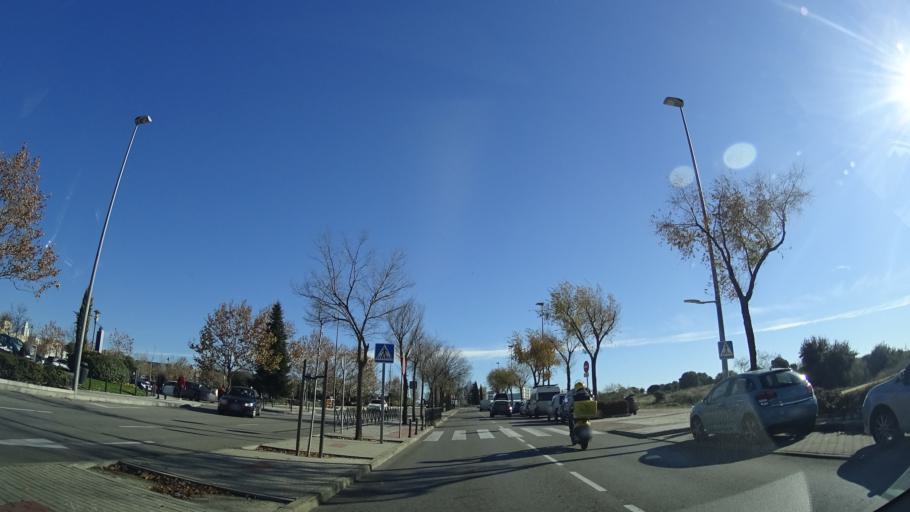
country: ES
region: Madrid
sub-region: Provincia de Madrid
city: Las Rozas de Madrid
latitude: 40.5170
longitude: -3.9020
